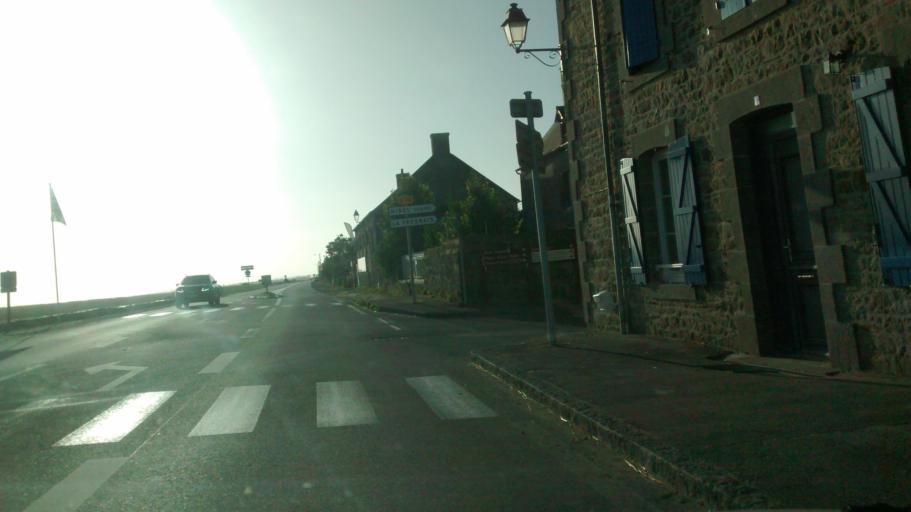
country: FR
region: Brittany
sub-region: Departement d'Ille-et-Vilaine
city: Hirel
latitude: 48.6069
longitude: -1.8014
